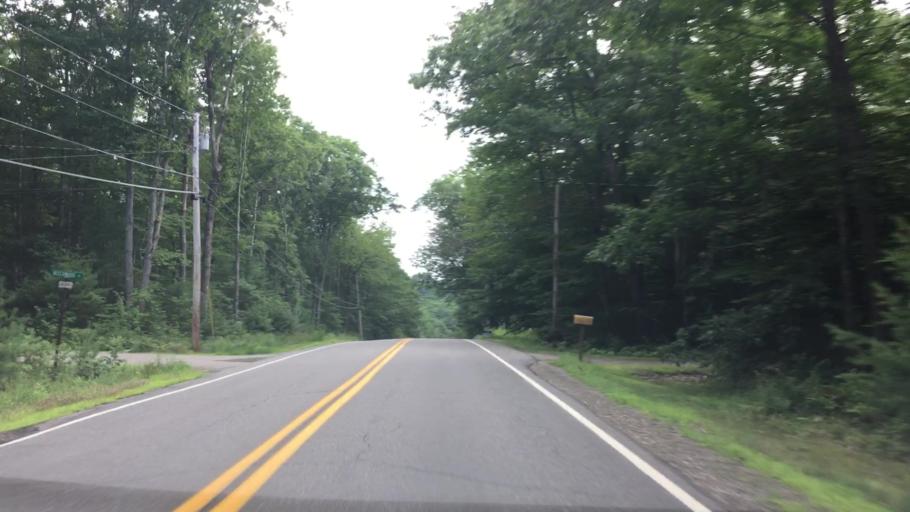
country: US
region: Maine
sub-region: Waldo County
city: Lincolnville
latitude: 44.3341
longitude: -69.0577
